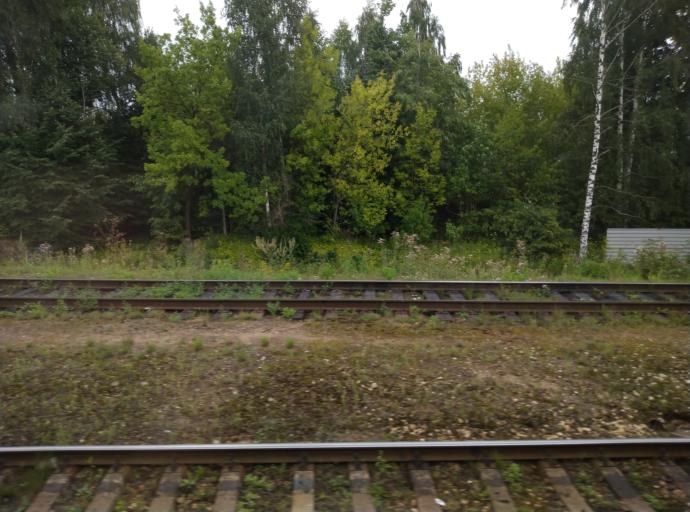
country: RU
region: Kostroma
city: Oktyabr'skiy
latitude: 57.7548
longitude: 40.9793
